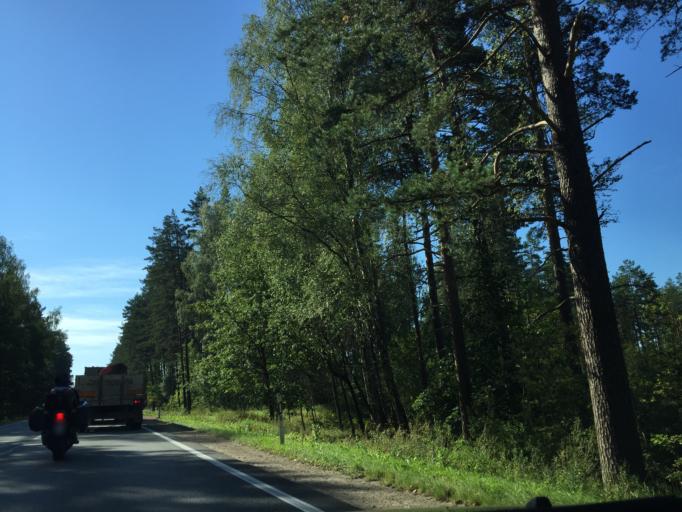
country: LV
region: Salaspils
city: Salaspils
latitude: 56.9475
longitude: 24.3800
